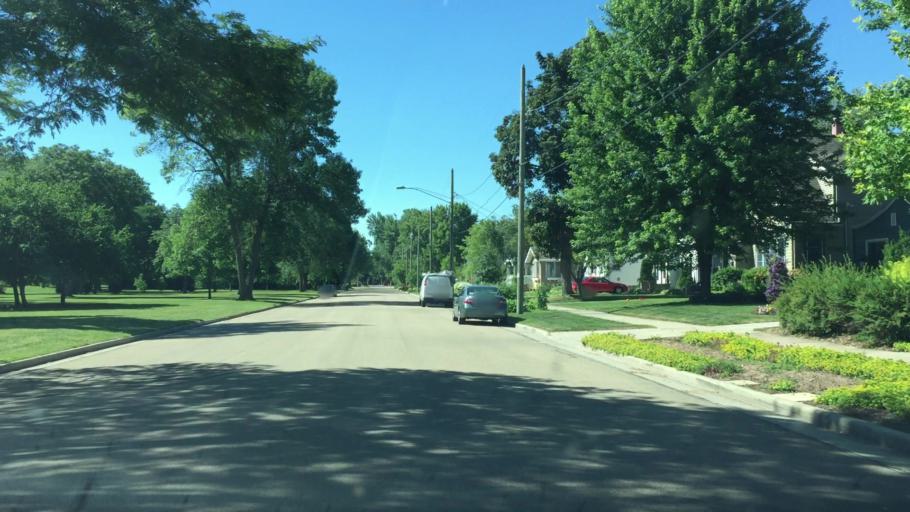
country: US
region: Wisconsin
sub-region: Winnebago County
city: Menasha
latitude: 44.1963
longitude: -88.4421
